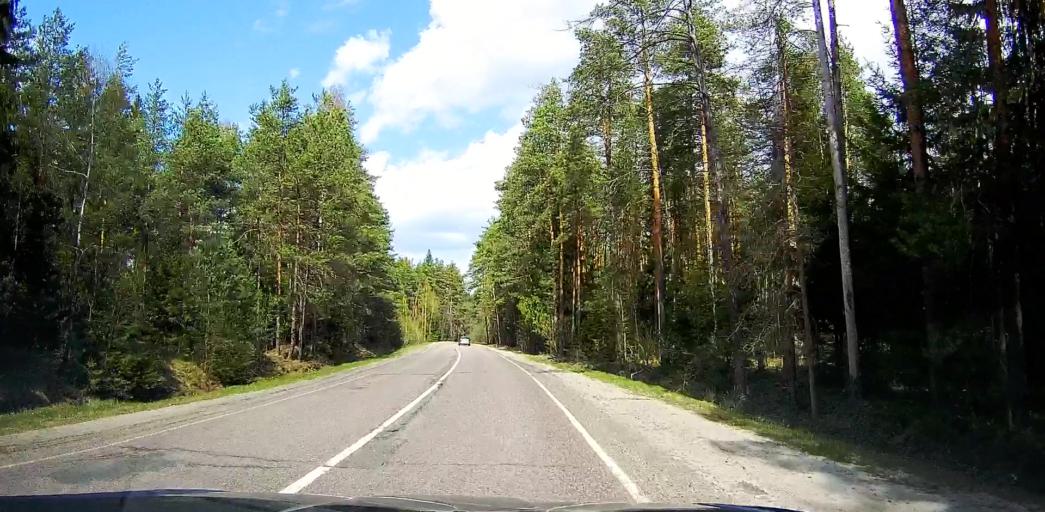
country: RU
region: Moskovskaya
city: Davydovo
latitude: 55.5675
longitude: 38.8217
